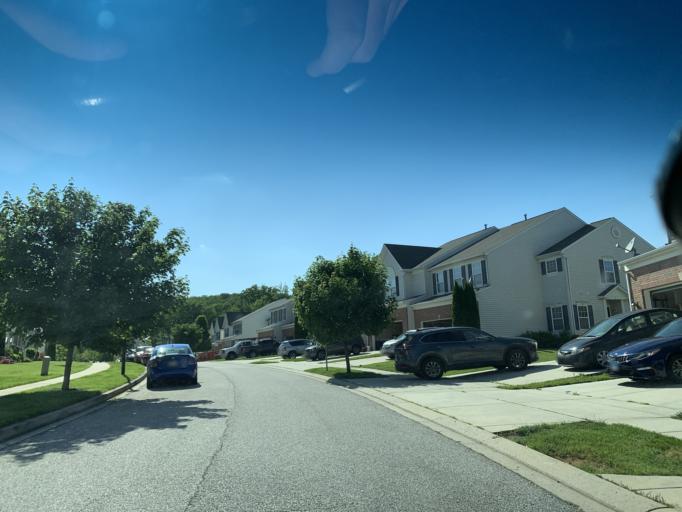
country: US
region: Maryland
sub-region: Harford County
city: Riverside
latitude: 39.4957
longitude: -76.2215
